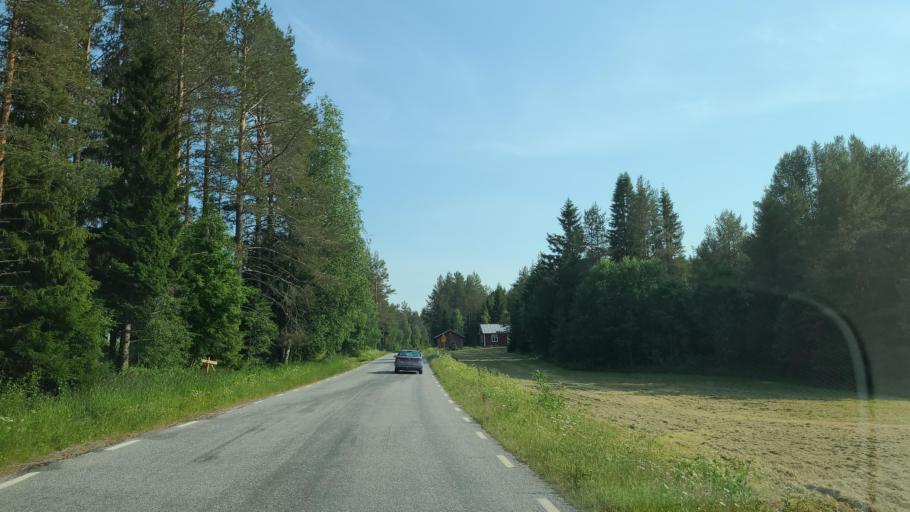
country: SE
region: Vaesterbotten
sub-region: Skelleftea Kommun
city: Burea
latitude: 64.3575
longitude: 21.3378
